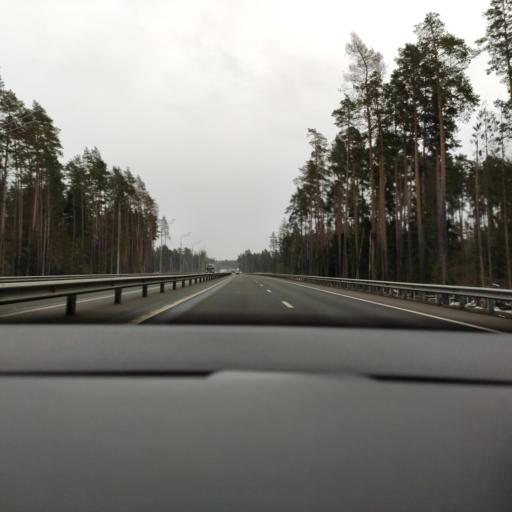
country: RU
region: Moskovskaya
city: Bol'shiye Vyazemy
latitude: 55.6633
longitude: 36.9459
